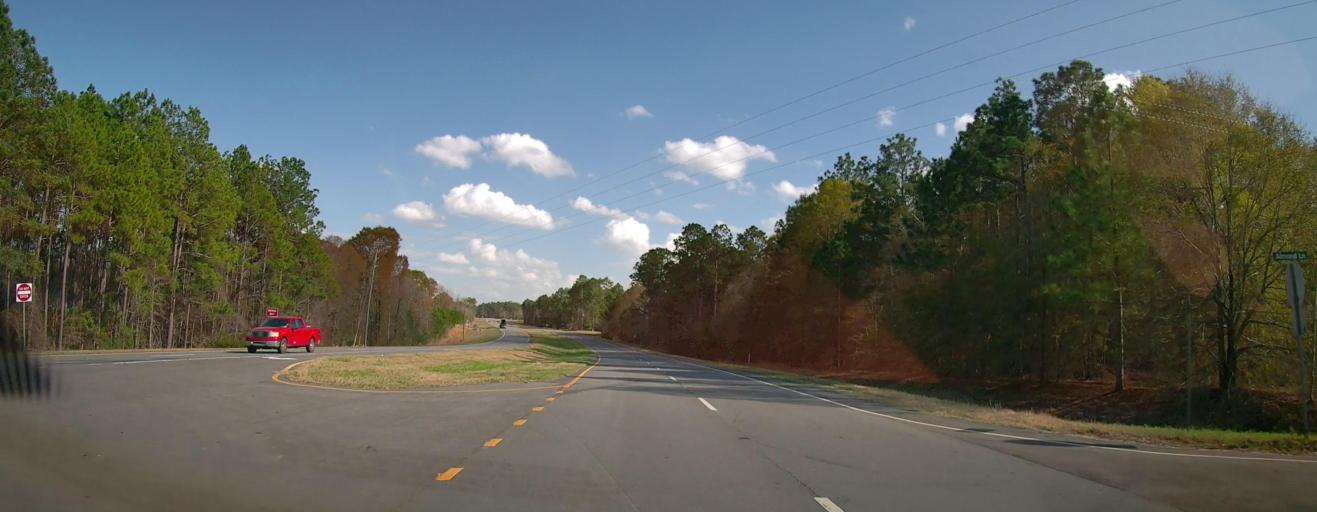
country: US
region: Georgia
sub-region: Telfair County
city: McRae
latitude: 32.0444
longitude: -82.8557
